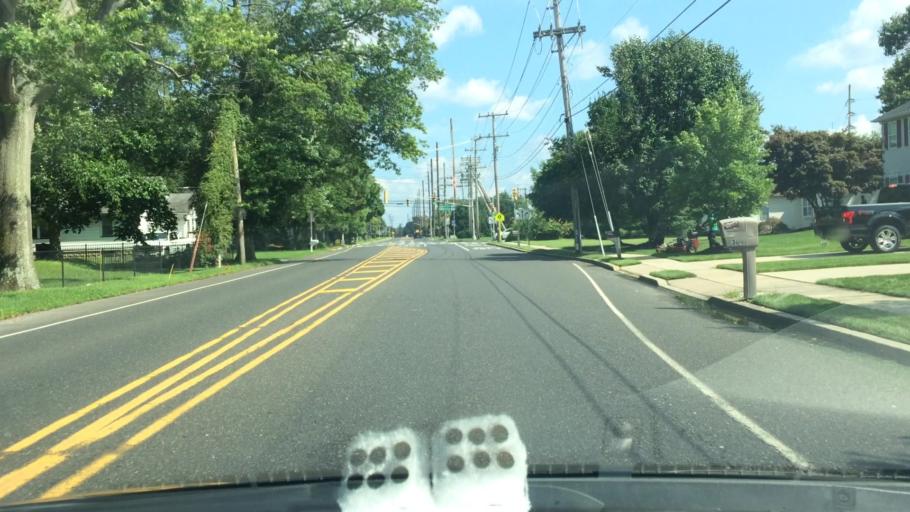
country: US
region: New Jersey
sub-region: Gloucester County
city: Turnersville
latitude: 39.7788
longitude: -75.0606
